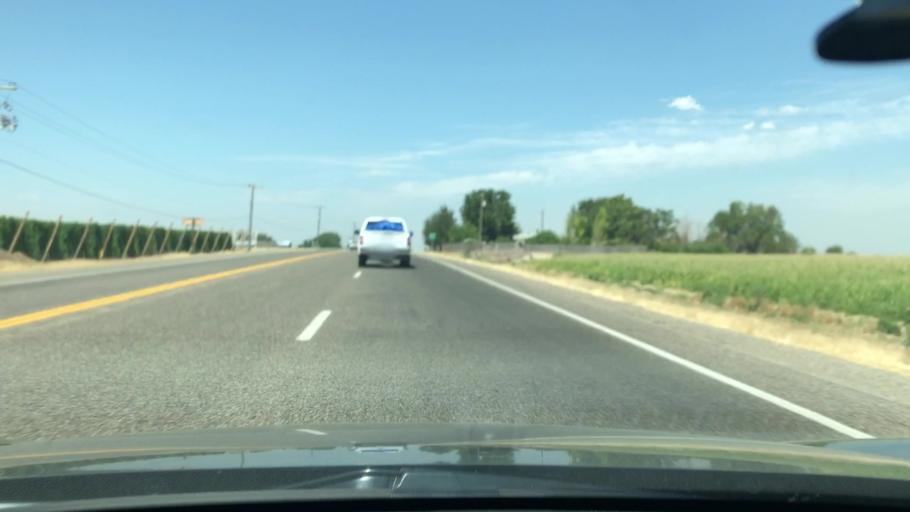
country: US
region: Idaho
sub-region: Canyon County
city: Wilder
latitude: 43.6624
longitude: -116.9118
